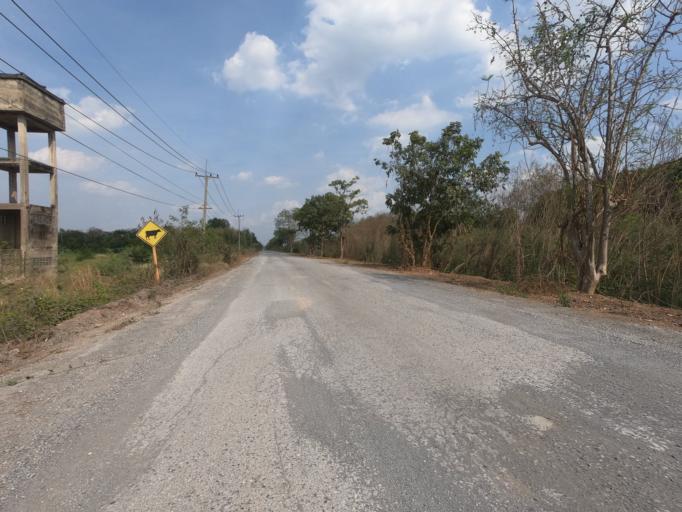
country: TH
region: Sara Buri
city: Nong Khae
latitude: 14.2548
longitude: 100.8467
